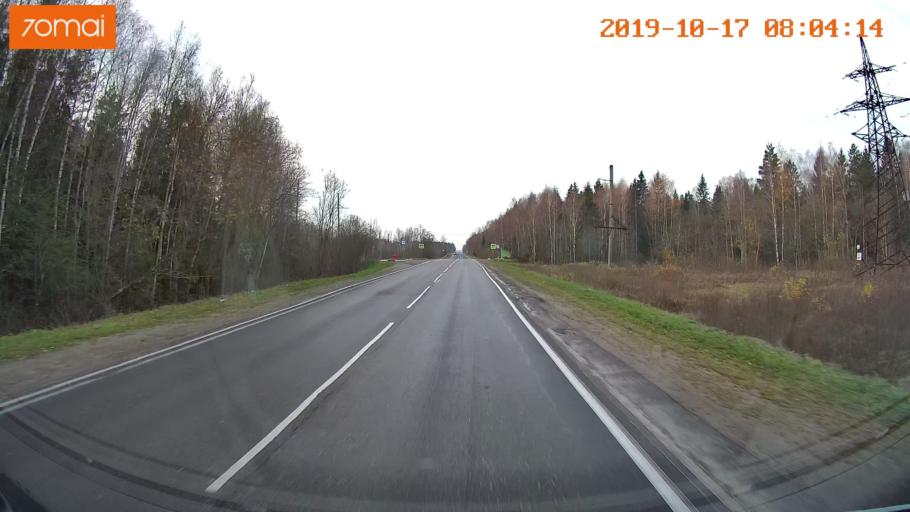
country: RU
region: Vladimir
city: Belaya Rechka
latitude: 56.3475
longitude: 39.4391
